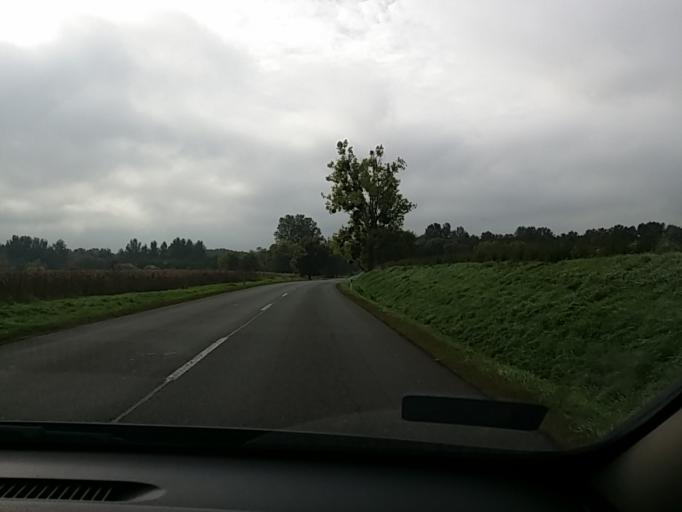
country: HU
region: Somogy
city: Karad
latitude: 46.5387
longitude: 17.8162
